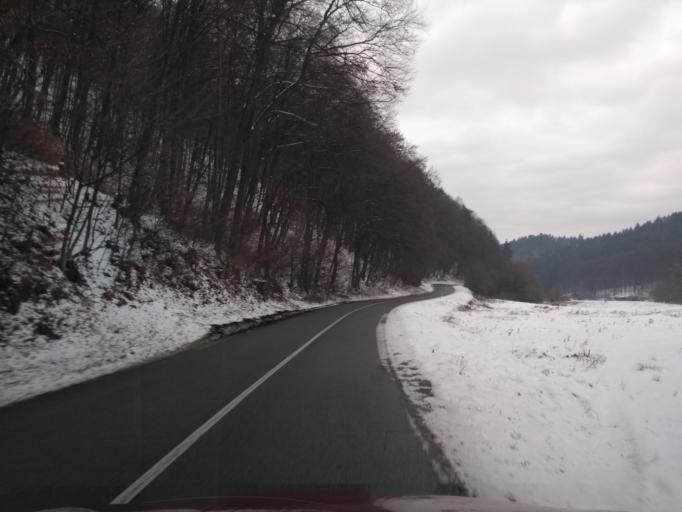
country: SK
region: Presovsky
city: Sabinov
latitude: 48.9643
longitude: 21.0977
